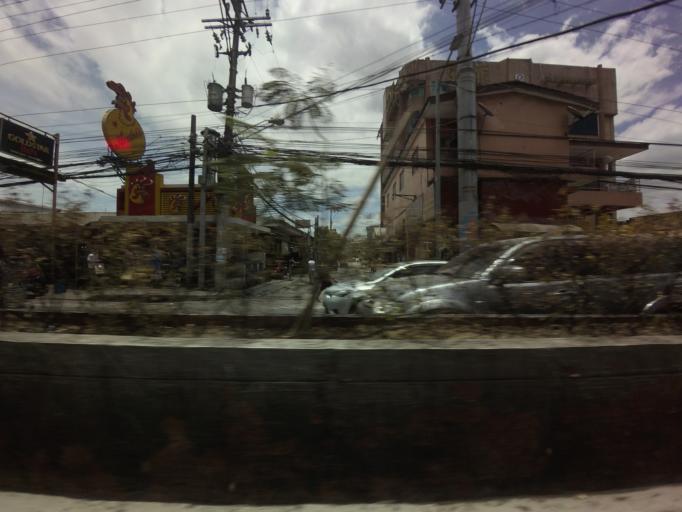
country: PH
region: Metro Manila
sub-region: Marikina
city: Calumpang
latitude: 14.6186
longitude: 121.1017
